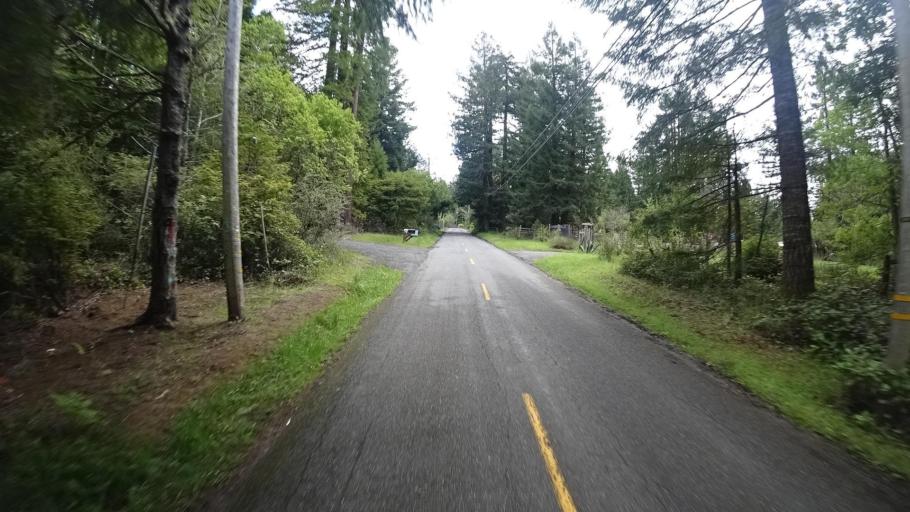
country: US
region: California
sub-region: Humboldt County
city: Bayside
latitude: 40.7910
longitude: -124.0203
